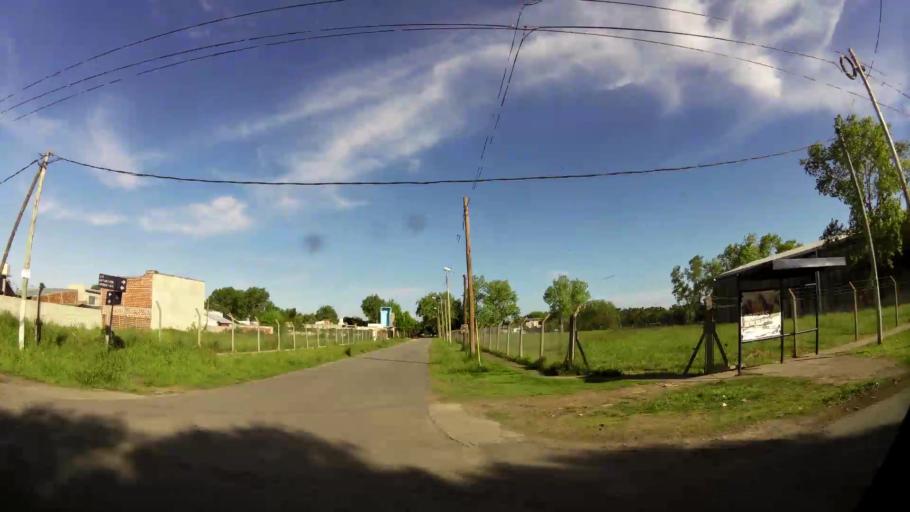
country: AR
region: Buenos Aires
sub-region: Partido de Quilmes
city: Quilmes
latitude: -34.7989
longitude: -58.2169
